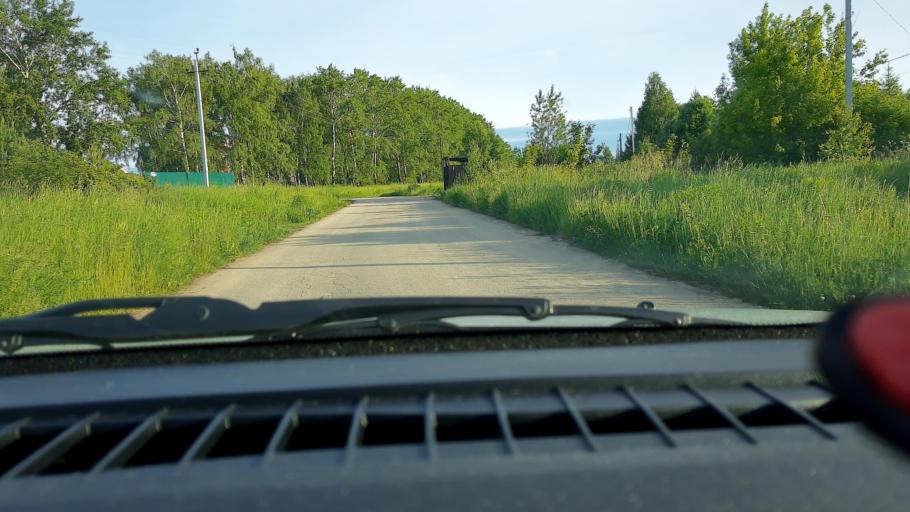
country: RU
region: Nizjnij Novgorod
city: Afonino
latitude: 56.1210
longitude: 44.0251
